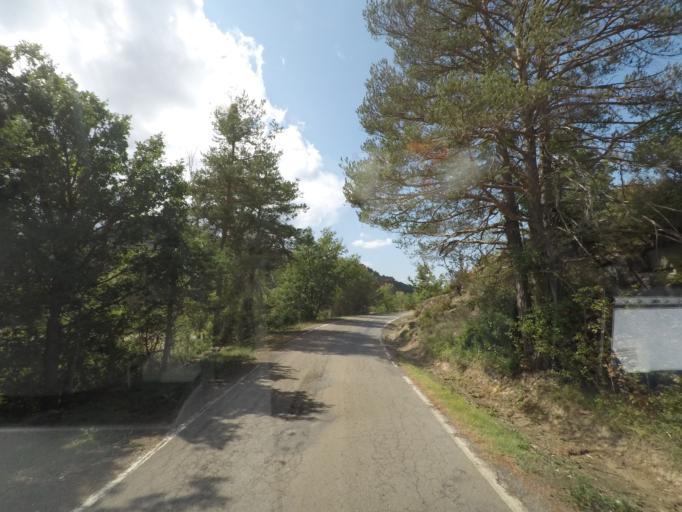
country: ES
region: Aragon
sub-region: Provincia de Huesca
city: Yebra de Basa
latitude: 42.3936
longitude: -0.3215
